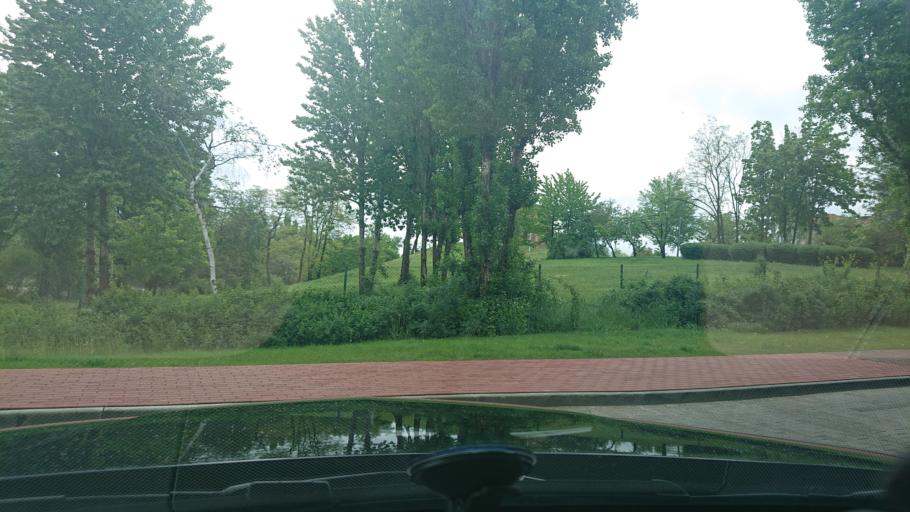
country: PL
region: Greater Poland Voivodeship
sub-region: Powiat gnieznienski
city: Gniezno
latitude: 52.5448
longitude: 17.6039
